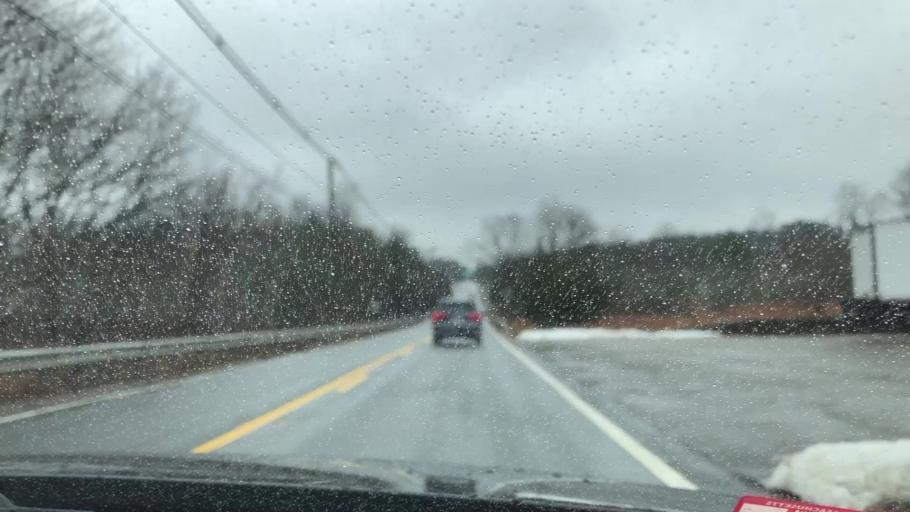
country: US
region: Massachusetts
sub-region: Norfolk County
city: Norfolk
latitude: 42.0939
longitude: -71.2955
